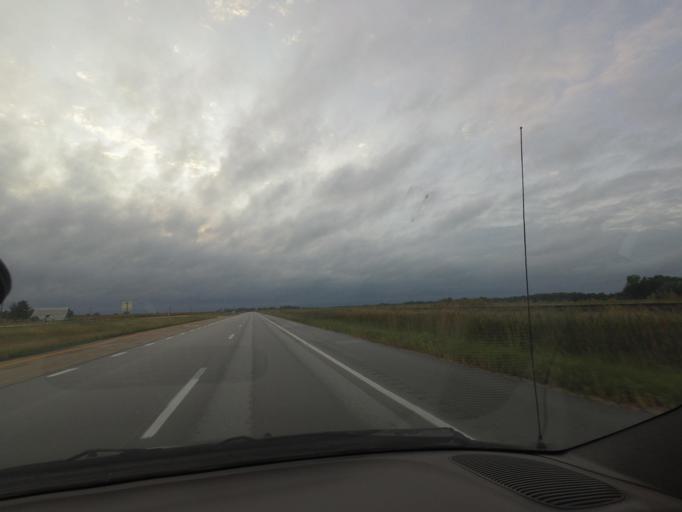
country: US
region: Missouri
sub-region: Shelby County
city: Shelbina
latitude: 39.6775
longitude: -91.9703
